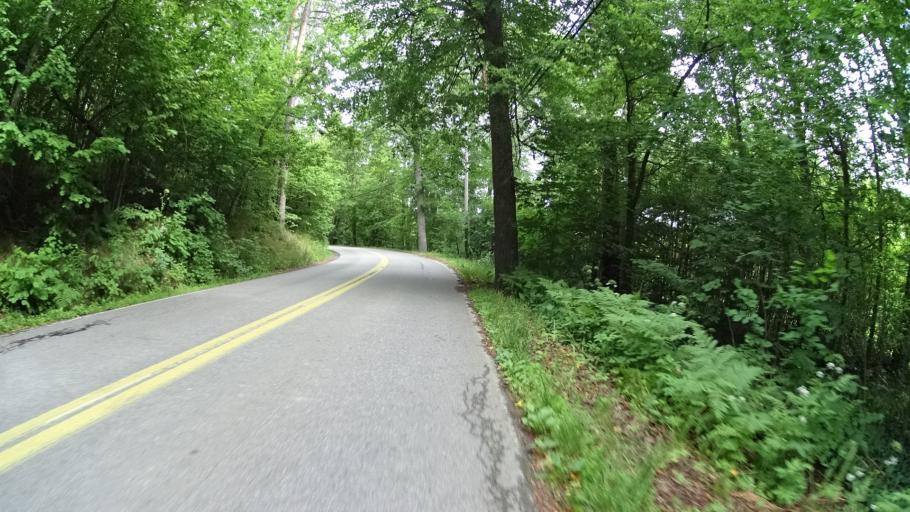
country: FI
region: Uusimaa
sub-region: Helsinki
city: Espoo
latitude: 60.2699
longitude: 24.6542
